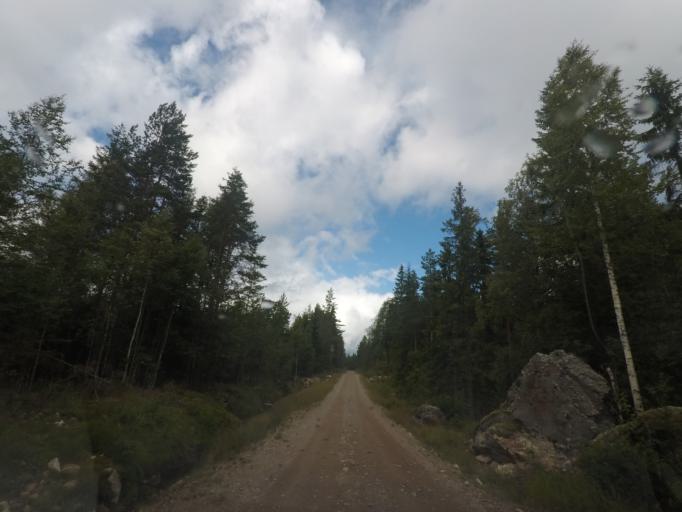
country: SE
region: Vaermland
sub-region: Filipstads Kommun
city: Lesjofors
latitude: 60.0833
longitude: 14.4212
